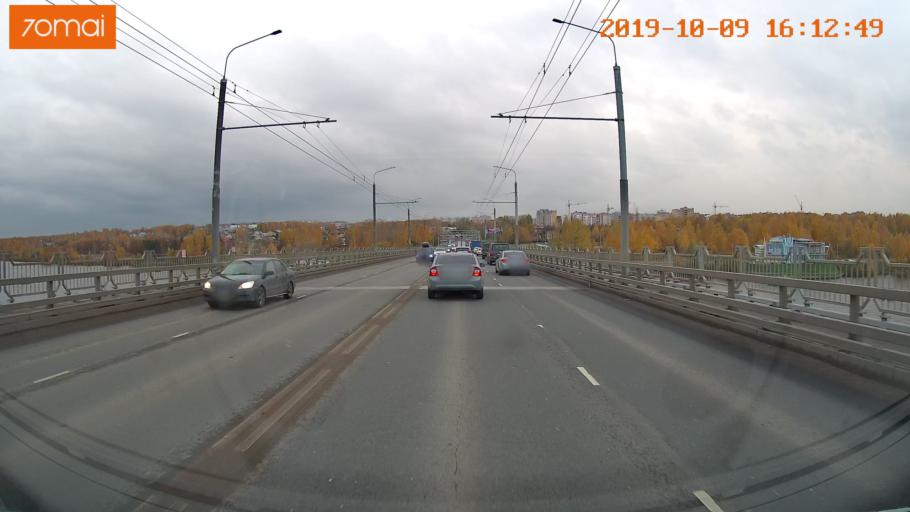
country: RU
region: Kostroma
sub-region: Kostromskoy Rayon
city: Kostroma
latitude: 57.7502
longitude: 40.9352
